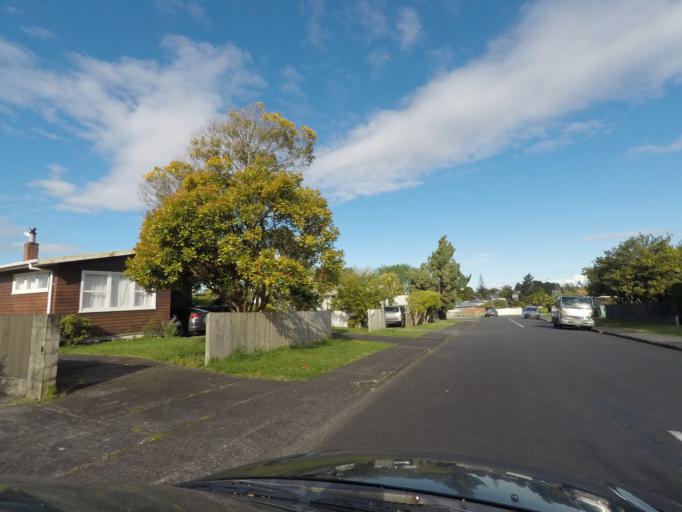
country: NZ
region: Auckland
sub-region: Auckland
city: Rosebank
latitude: -36.8828
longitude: 174.6524
